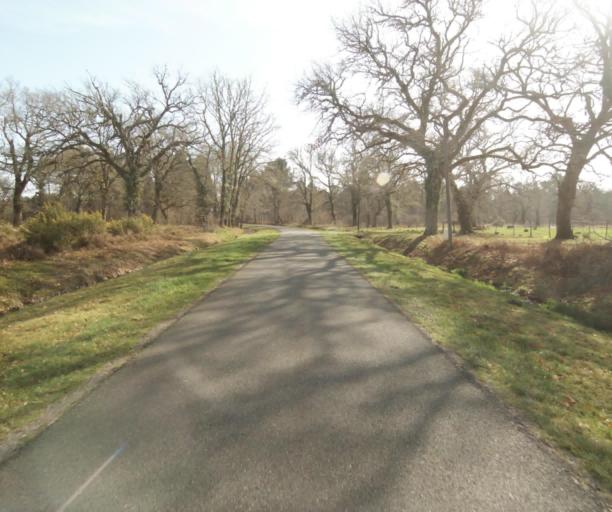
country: FR
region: Aquitaine
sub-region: Departement de la Gironde
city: Grignols
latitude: 44.2326
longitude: -0.1559
